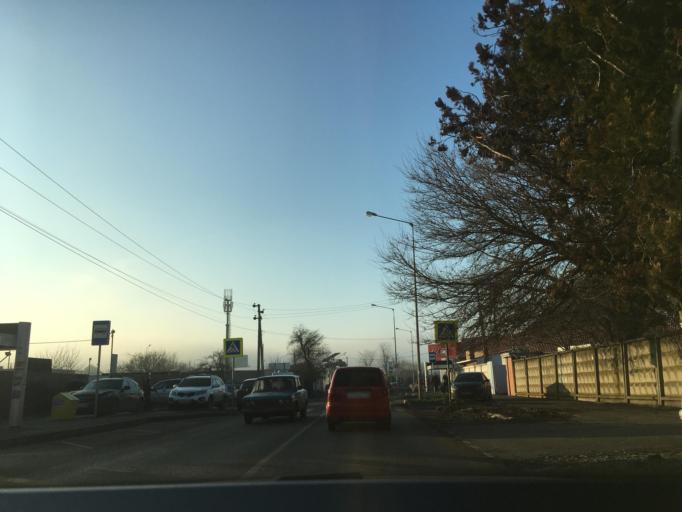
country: RU
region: Krasnodarskiy
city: Krasnodar
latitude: 45.1261
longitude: 39.0128
